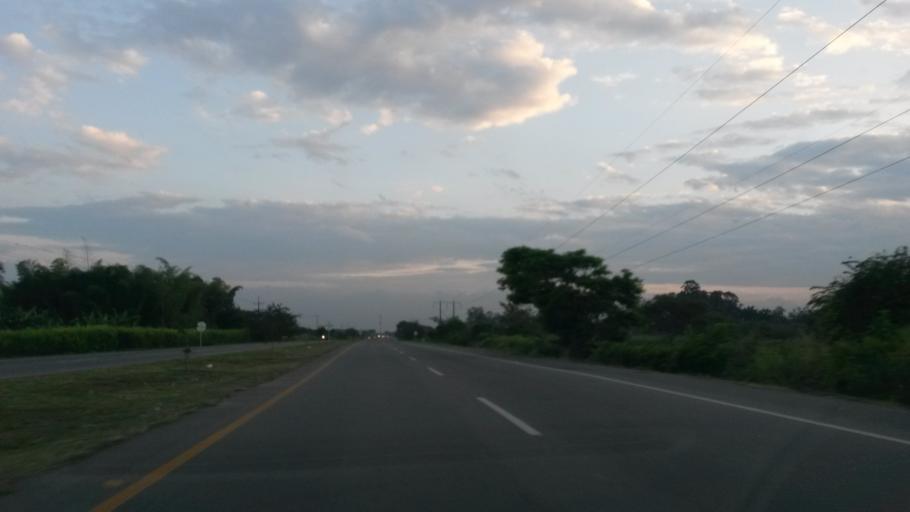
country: CO
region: Cauca
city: Santander de Quilichao
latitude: 3.0601
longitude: -76.4746
